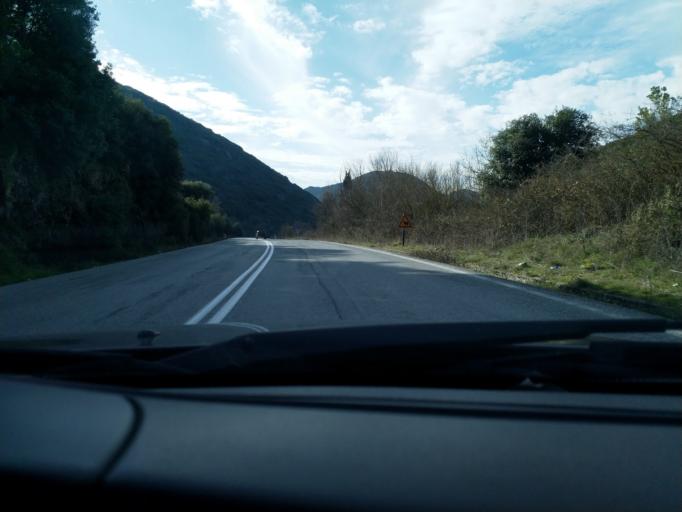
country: GR
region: Epirus
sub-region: Nomos Ioanninon
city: Agia Kyriaki
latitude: 39.5007
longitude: 20.8797
